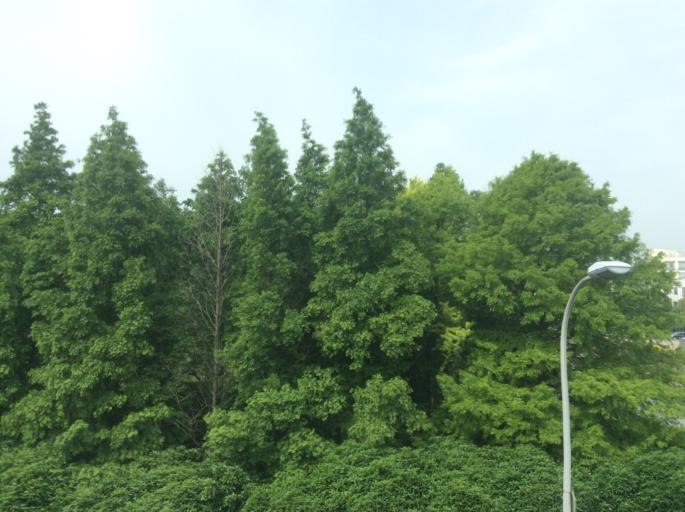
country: CN
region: Shanghai Shi
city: Laogang
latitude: 31.1807
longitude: 121.7846
